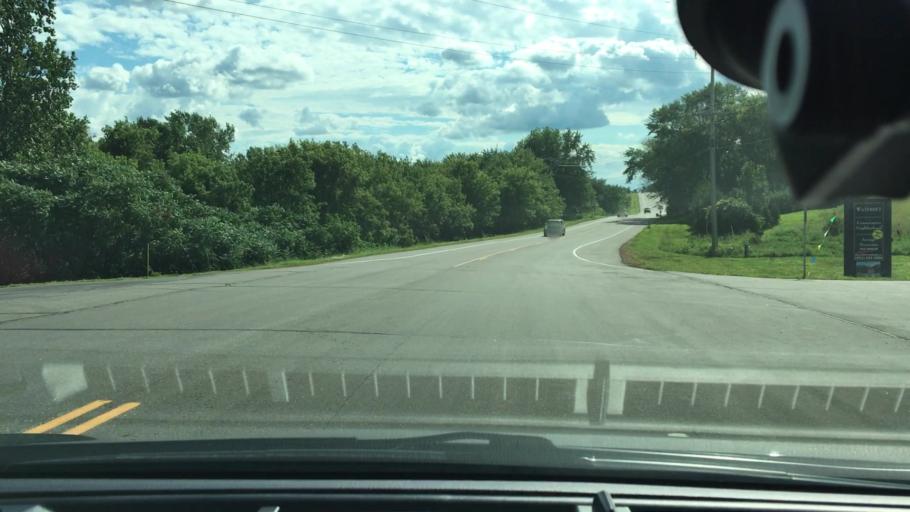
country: US
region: Minnesota
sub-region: Hennepin County
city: Minnetrista
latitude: 44.9207
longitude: -93.7282
